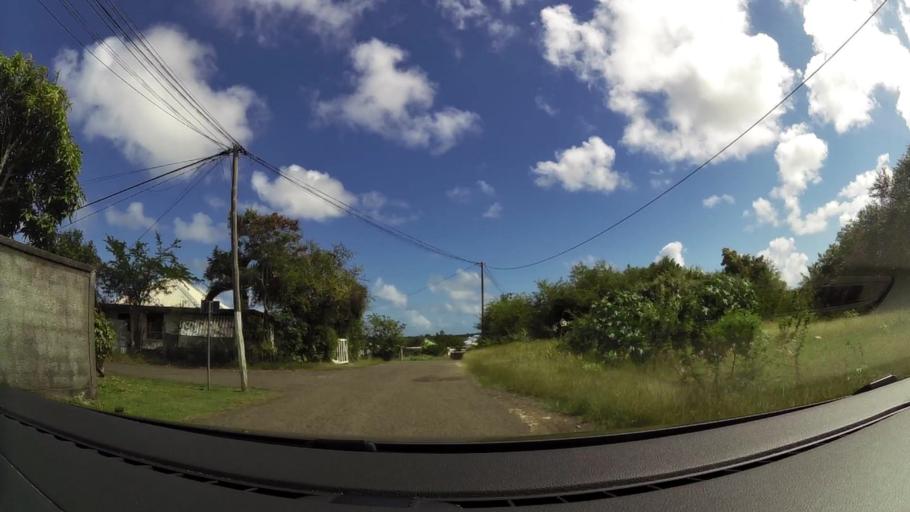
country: GP
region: Guadeloupe
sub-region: Guadeloupe
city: Anse-Bertrand
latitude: 16.4655
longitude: -61.5028
